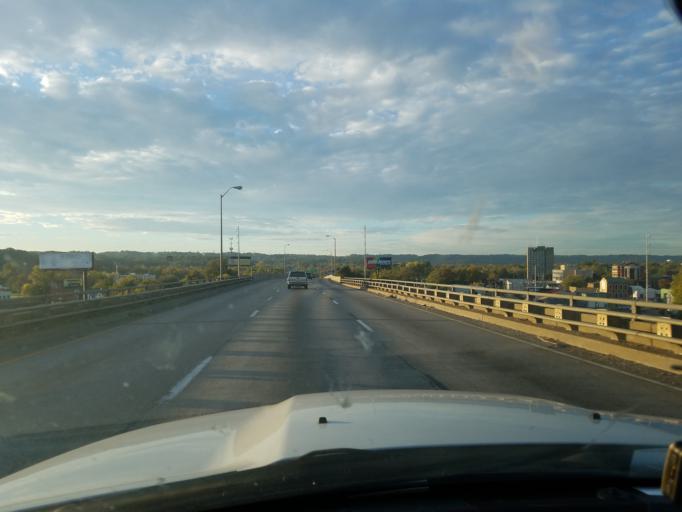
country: US
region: Indiana
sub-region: Floyd County
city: New Albany
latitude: 38.2807
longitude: -85.8242
